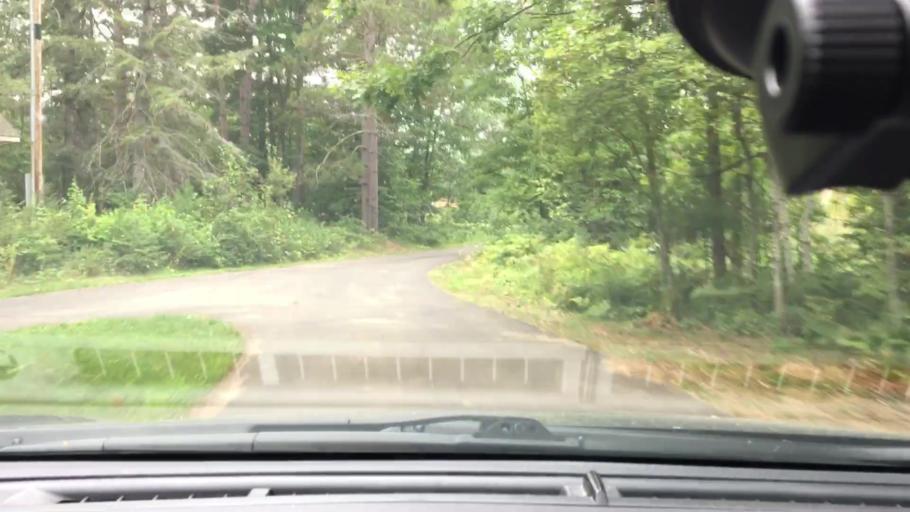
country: US
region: Minnesota
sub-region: Crow Wing County
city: Cross Lake
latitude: 46.8263
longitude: -93.9464
